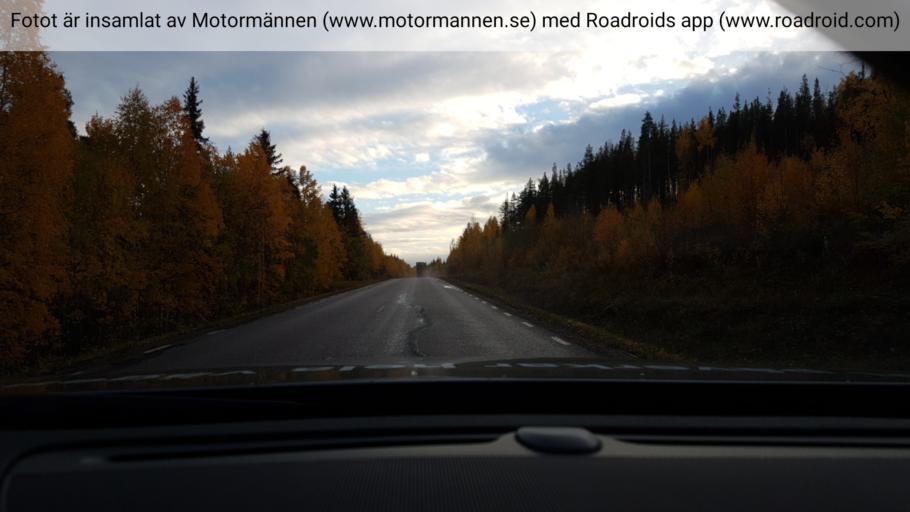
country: SE
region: Norrbotten
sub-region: Overkalix Kommun
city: OEverkalix
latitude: 66.8005
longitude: 22.7315
